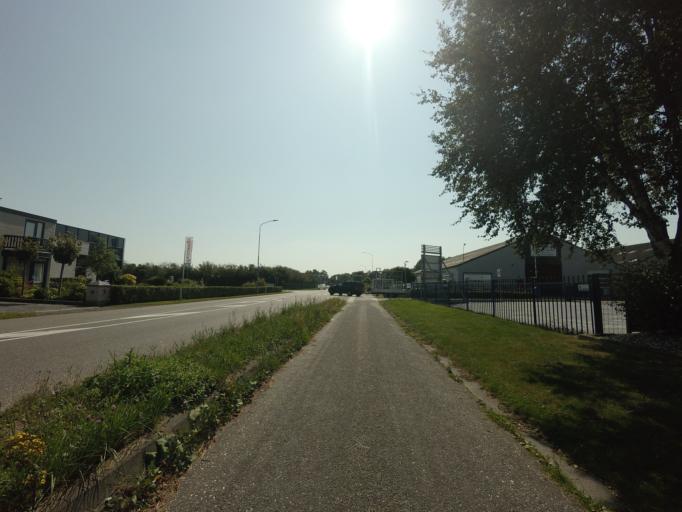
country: NL
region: Groningen
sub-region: Gemeente Zuidhorn
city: Grijpskerk
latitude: 53.2669
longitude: 6.3068
